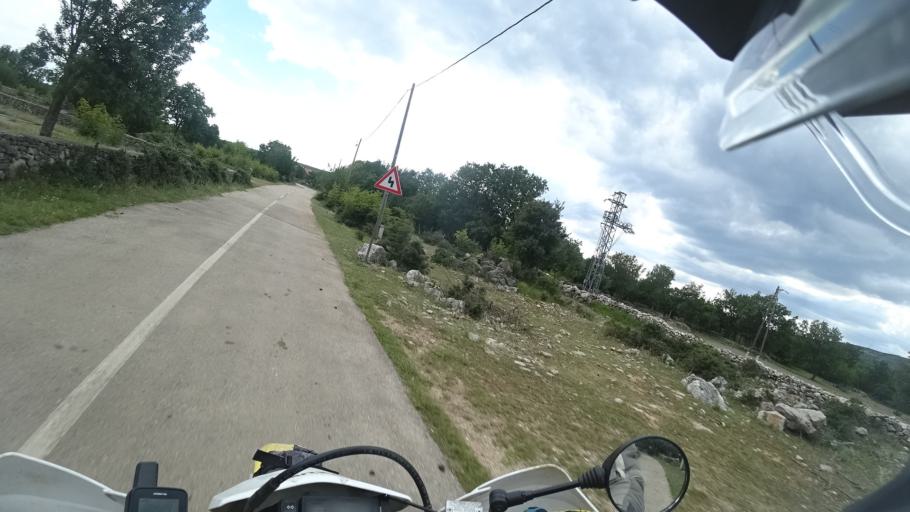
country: HR
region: Zadarska
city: Gracac
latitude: 44.1908
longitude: 15.9074
